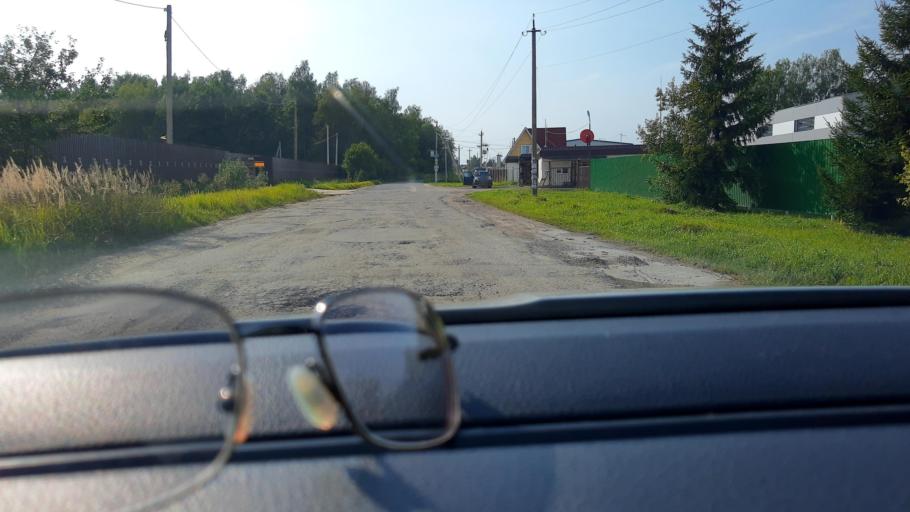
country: RU
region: Kaluga
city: Balabanovo
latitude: 55.1476
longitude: 36.6670
